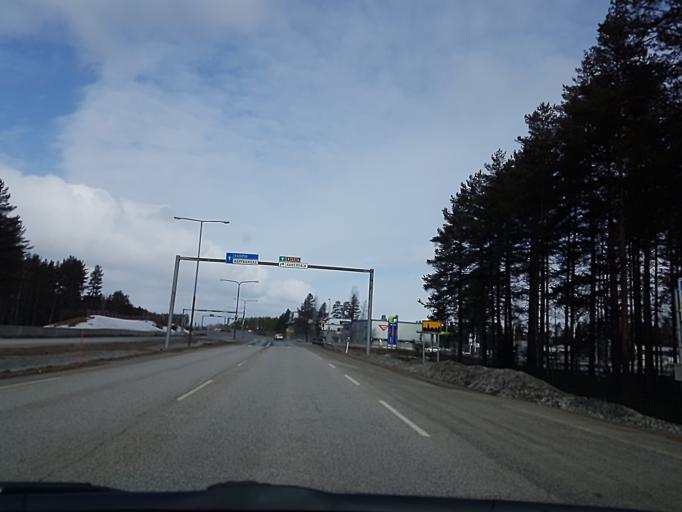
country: FI
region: North Karelia
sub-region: Joensuu
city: Joensuu
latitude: 62.6131
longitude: 29.7391
